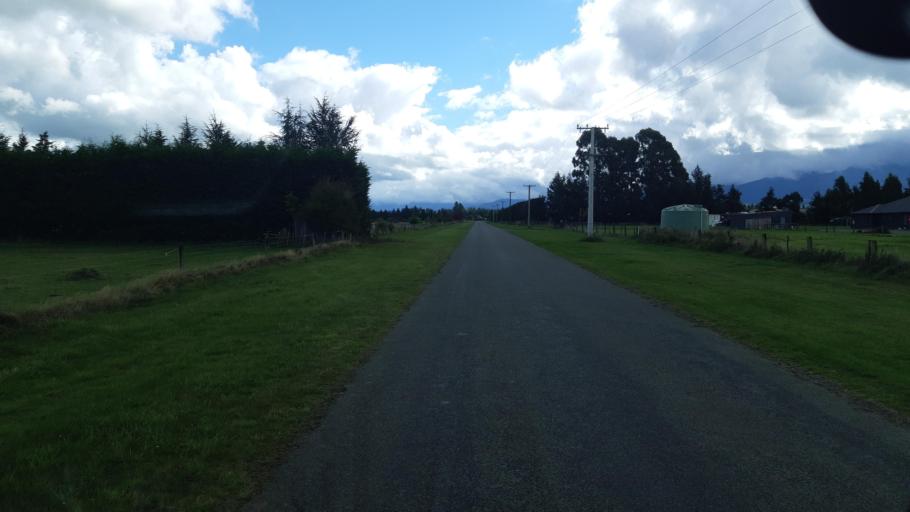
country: NZ
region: Canterbury
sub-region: Waimakariri District
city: Oxford
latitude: -43.3121
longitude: 172.1623
